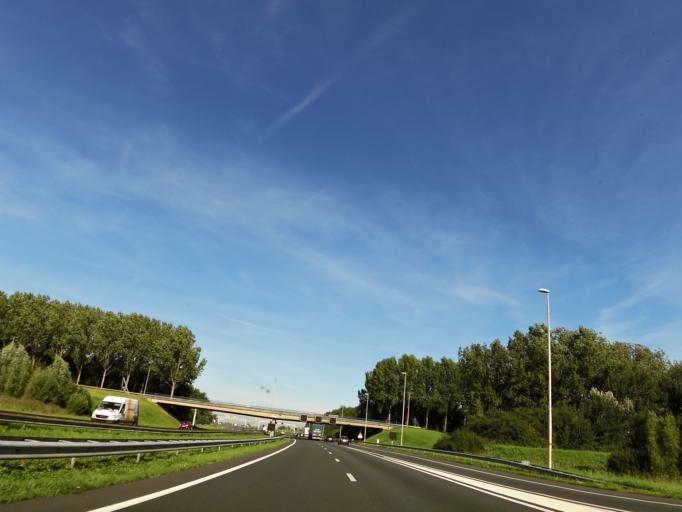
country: NL
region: Zeeland
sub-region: Gemeente Reimerswaal
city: Yerseke
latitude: 51.4623
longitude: 4.0269
